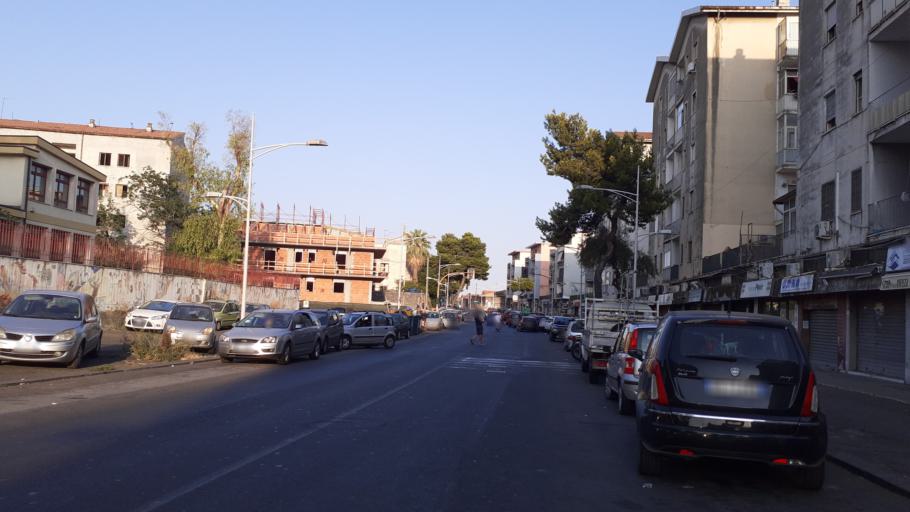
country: IT
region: Sicily
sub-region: Catania
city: Catania
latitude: 37.5022
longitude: 15.0604
